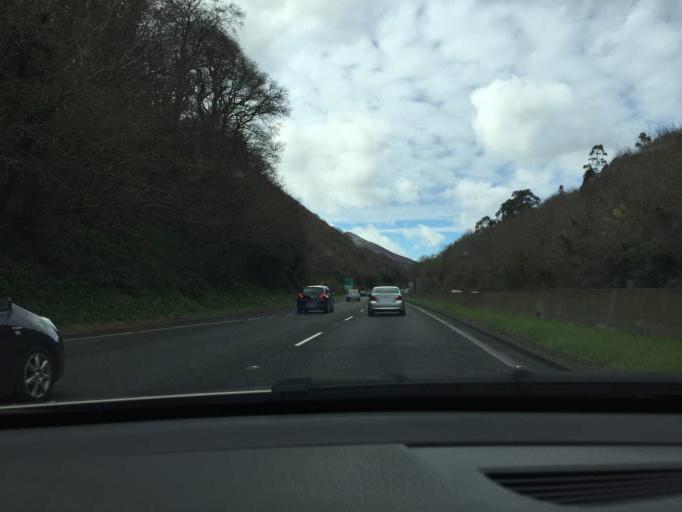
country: IE
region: Leinster
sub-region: Wicklow
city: Kilpedder
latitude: 53.1324
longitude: -6.1107
